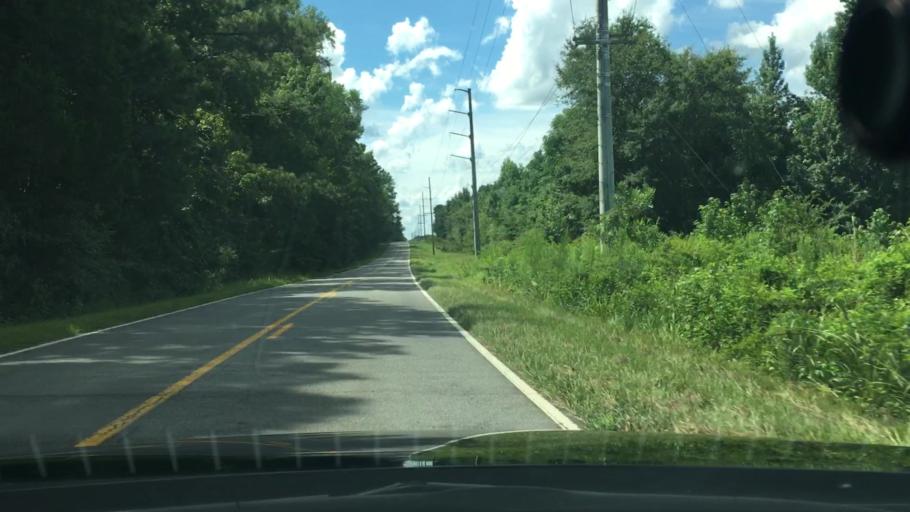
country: US
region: Georgia
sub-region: Putnam County
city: Jefferson
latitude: 33.3675
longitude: -83.2853
